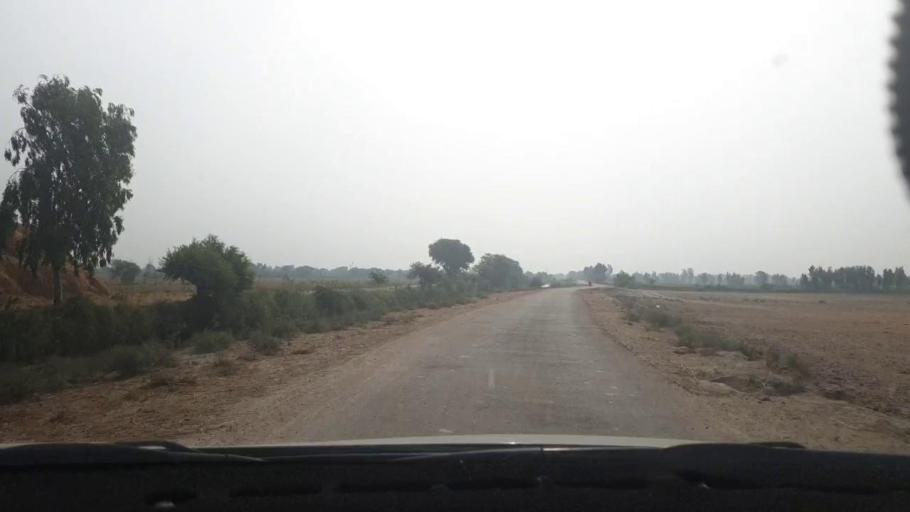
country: PK
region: Sindh
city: Tando Muhammad Khan
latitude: 25.0542
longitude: 68.5492
